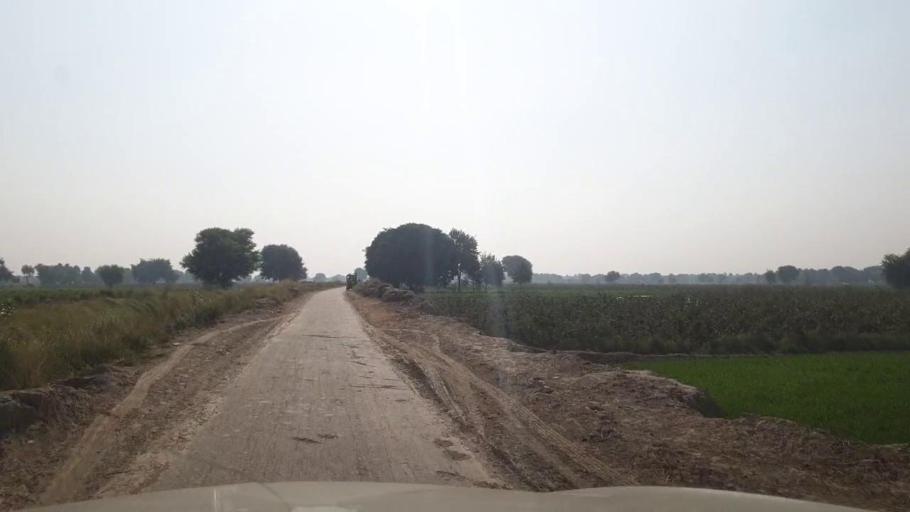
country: PK
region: Sindh
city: Bhan
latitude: 26.5264
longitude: 67.7789
